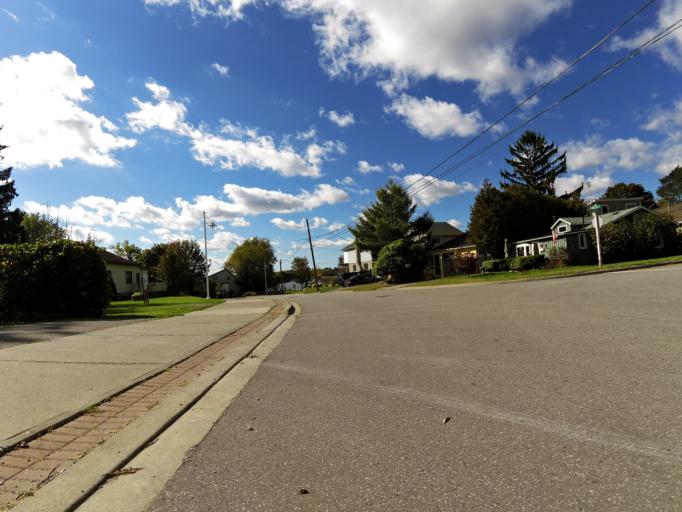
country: CA
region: Ontario
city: Ajax
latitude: 43.8165
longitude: -79.0834
